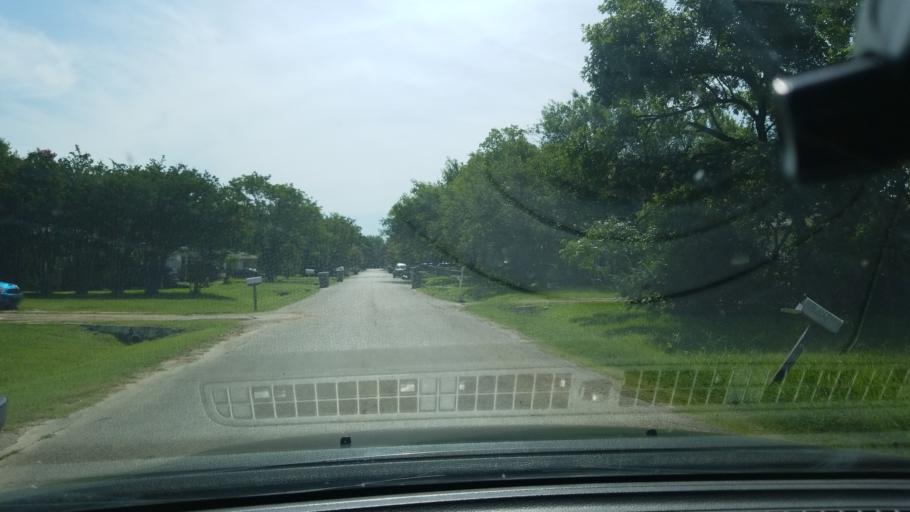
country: US
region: Texas
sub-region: Dallas County
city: Balch Springs
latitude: 32.7309
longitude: -96.6258
